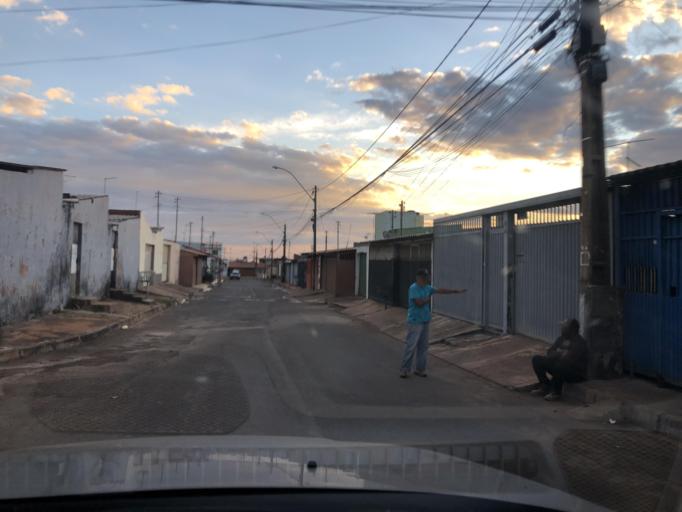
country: BR
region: Federal District
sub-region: Brasilia
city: Brasilia
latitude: -15.8772
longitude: -48.0975
